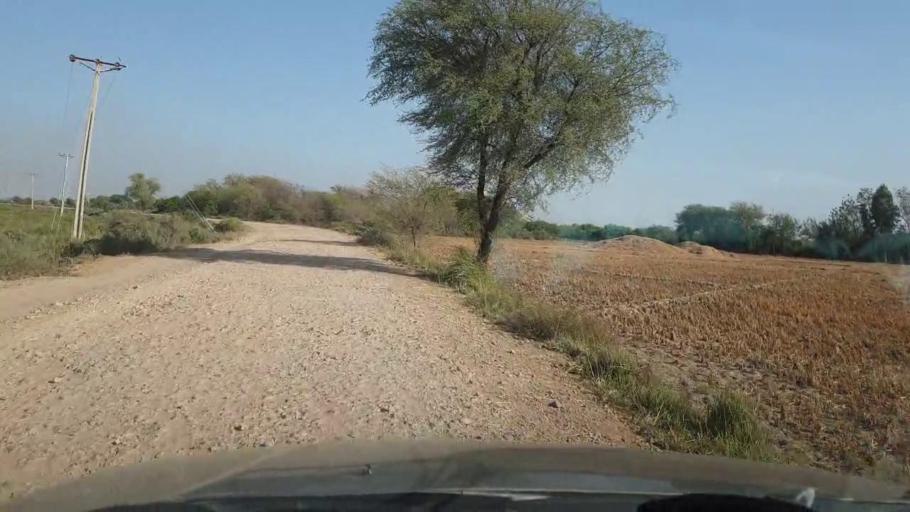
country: PK
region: Sindh
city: Bulri
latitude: 25.1084
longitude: 68.2510
